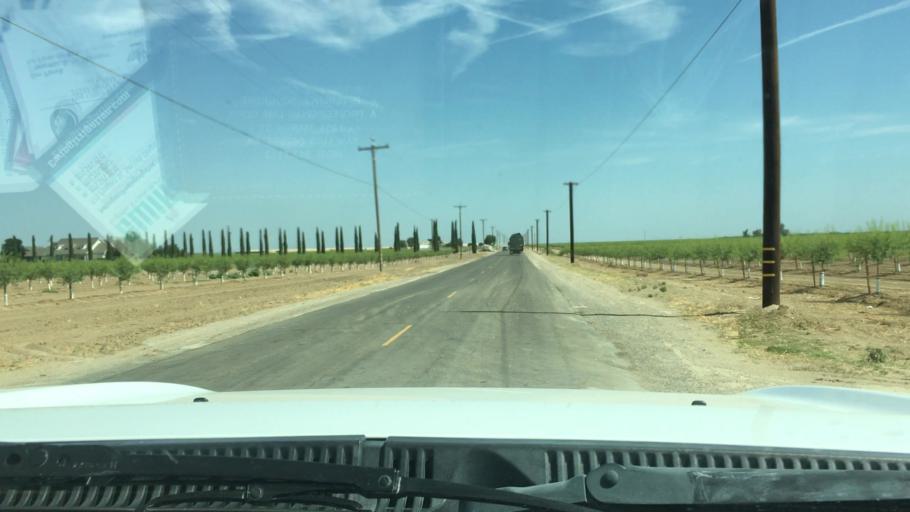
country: US
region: California
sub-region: Kern County
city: Shafter
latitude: 35.4565
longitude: -119.3681
